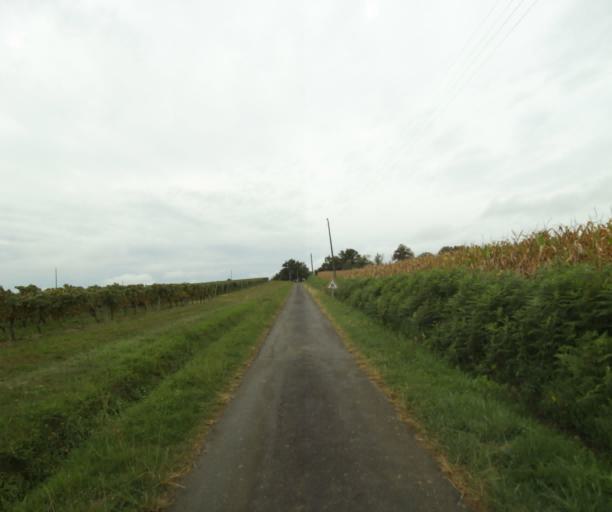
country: FR
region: Midi-Pyrenees
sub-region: Departement du Gers
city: Cazaubon
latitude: 43.8722
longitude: -0.0661
